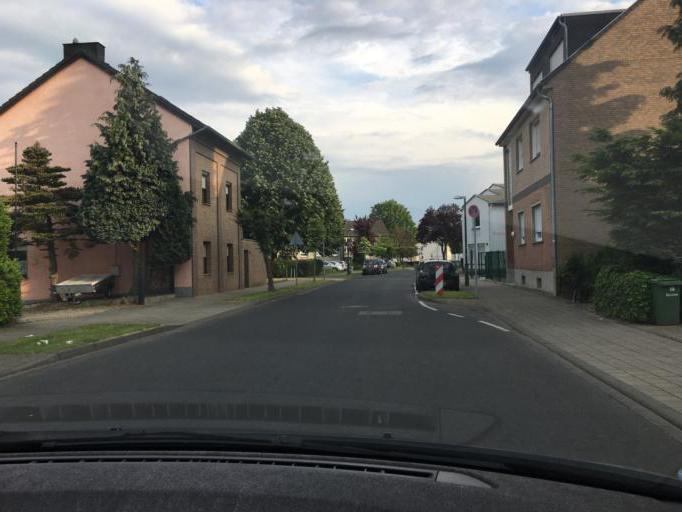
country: DE
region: North Rhine-Westphalia
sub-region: Regierungsbezirk Koln
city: Dueren
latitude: 50.8180
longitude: 6.4767
